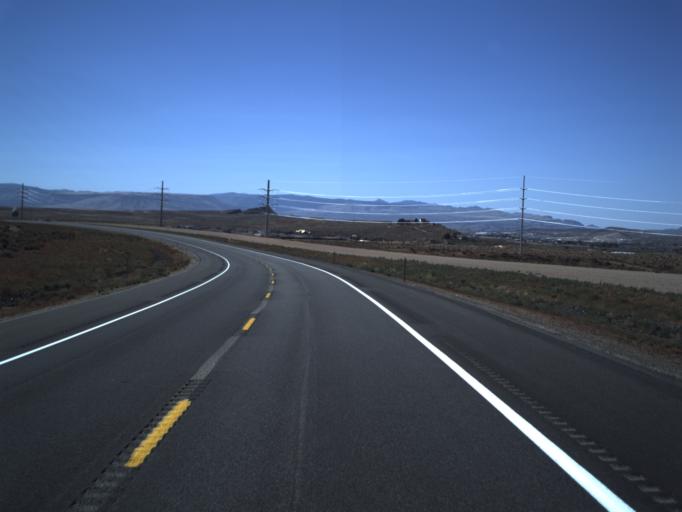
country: US
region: Utah
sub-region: Washington County
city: Washington
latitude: 37.0798
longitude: -113.4830
